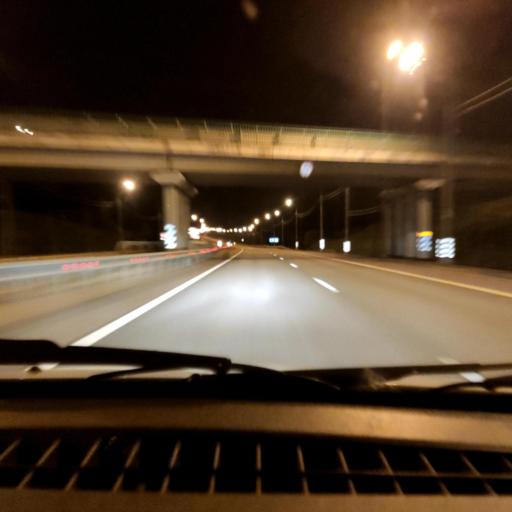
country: RU
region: Lipetsk
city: Zadonsk
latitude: 52.3295
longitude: 39.0161
